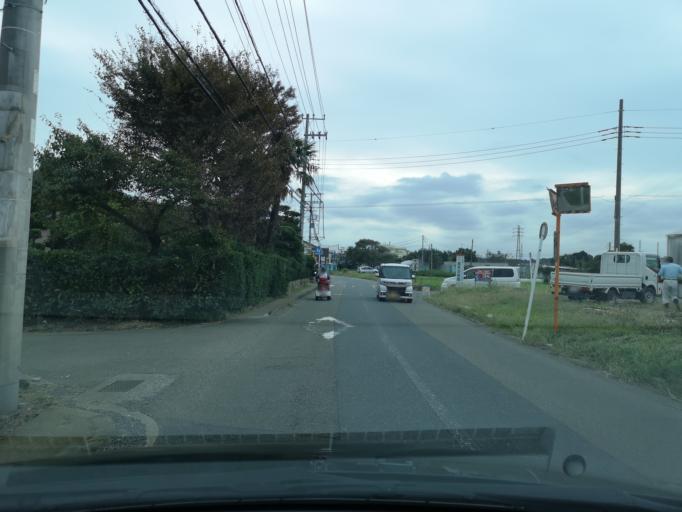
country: JP
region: Kanagawa
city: Chigasaki
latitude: 35.3856
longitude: 139.3957
